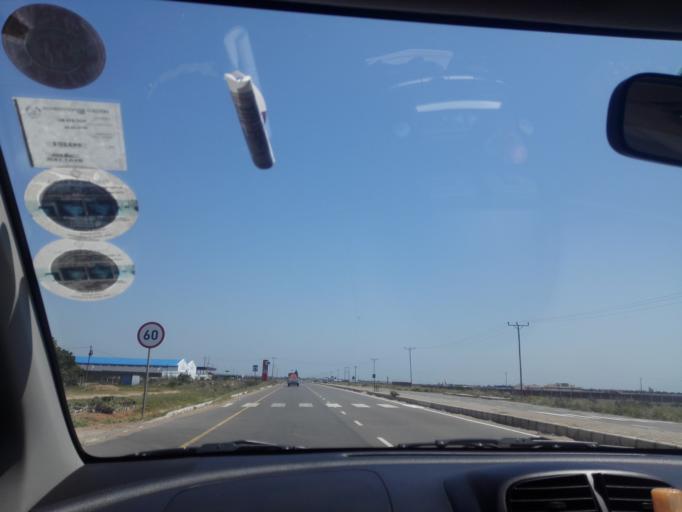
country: MZ
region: Maputo City
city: Maputo
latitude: -25.8447
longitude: 32.6714
